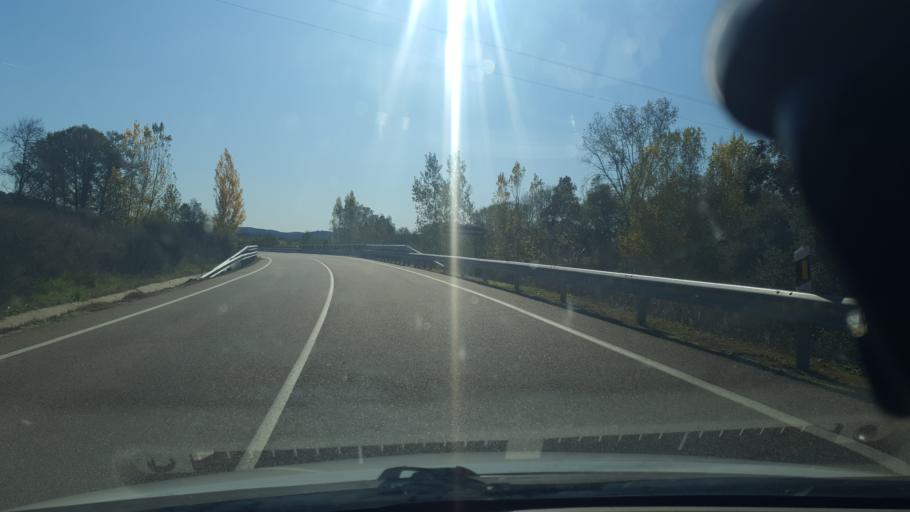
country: ES
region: Castille and Leon
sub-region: Provincia de Avila
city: Arenas de San Pedro
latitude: 40.1824
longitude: -5.0518
